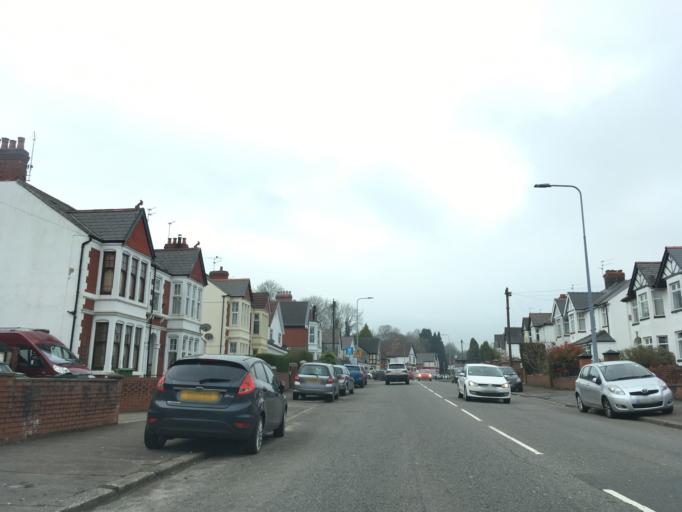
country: GB
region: Wales
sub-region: Cardiff
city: Cardiff
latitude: 51.5238
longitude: -3.1806
